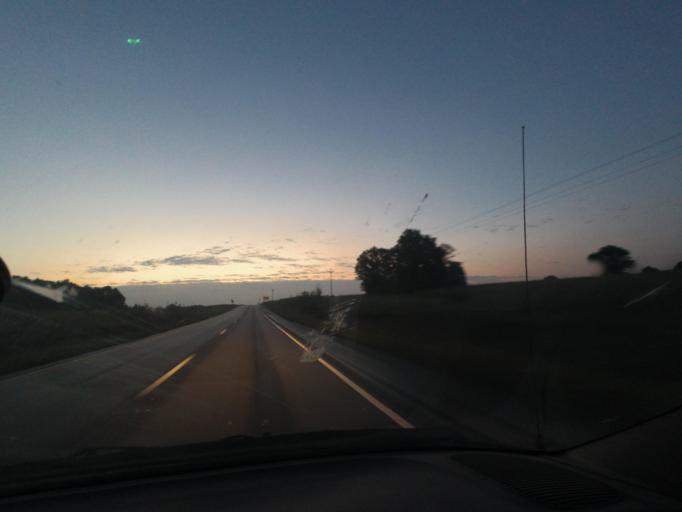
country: US
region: Missouri
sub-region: Linn County
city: Linneus
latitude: 39.7782
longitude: -93.1858
